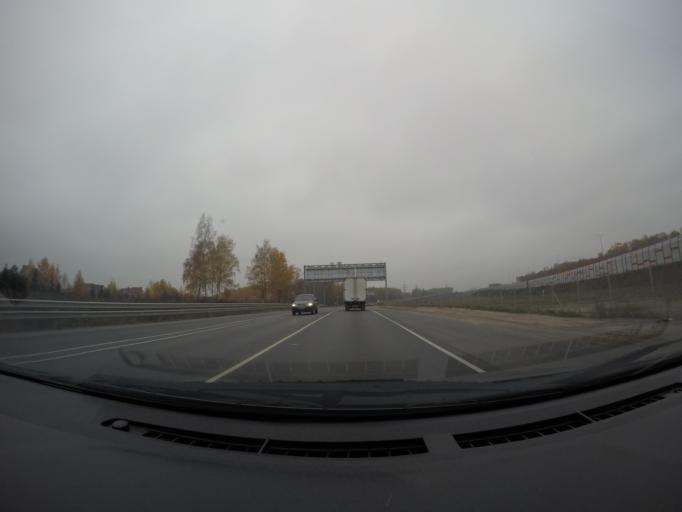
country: RU
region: Moskovskaya
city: Belyye Stolby
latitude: 55.3441
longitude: 37.8657
